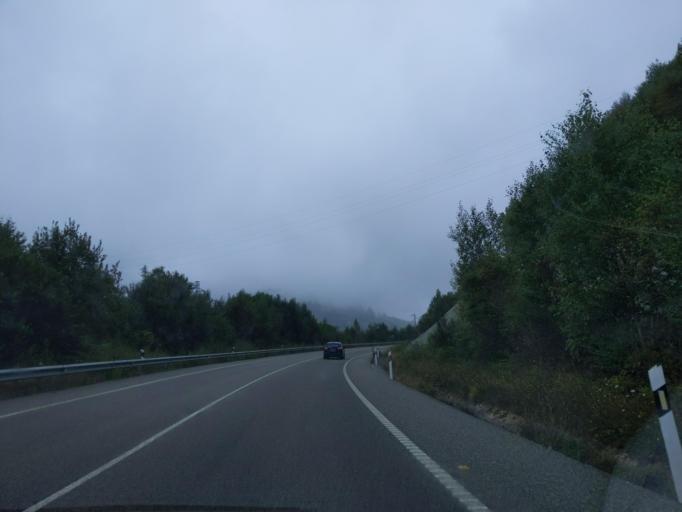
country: ES
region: Asturias
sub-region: Province of Asturias
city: El entrego
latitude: 43.2907
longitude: -5.6206
